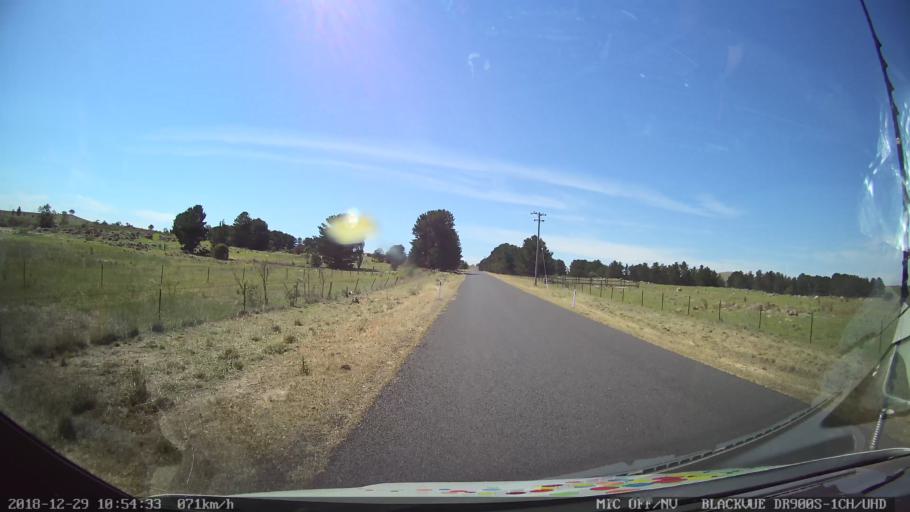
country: AU
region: New South Wales
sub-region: Palerang
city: Bungendore
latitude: -35.1156
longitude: 149.5277
